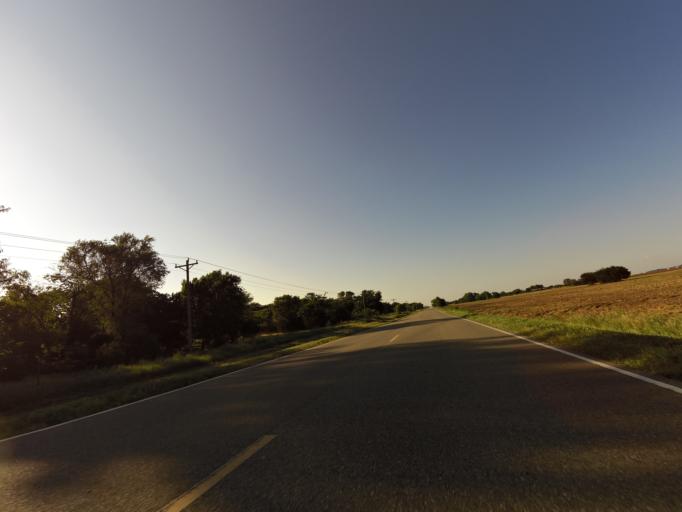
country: US
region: Kansas
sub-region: Reno County
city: Buhler
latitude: 38.1641
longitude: -97.8487
